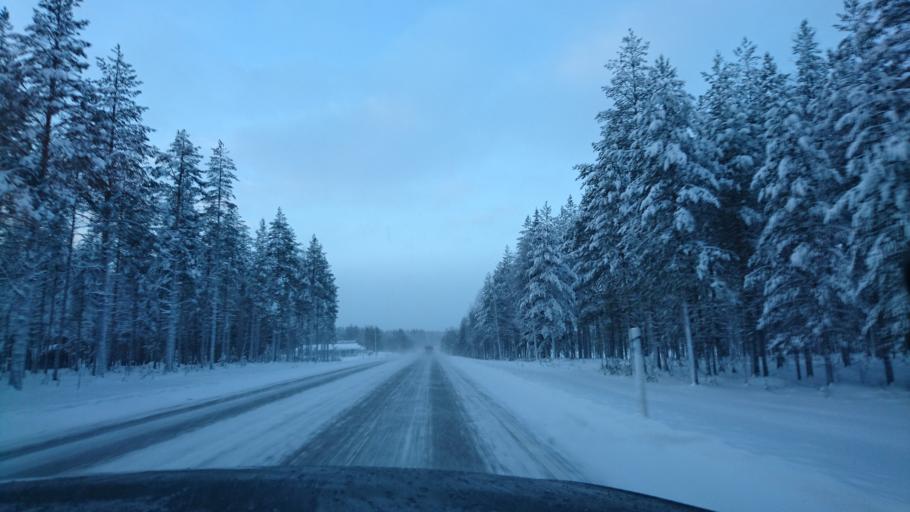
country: FI
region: Northern Ostrobothnia
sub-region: Koillismaa
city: Taivalkoski
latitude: 65.4869
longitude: 27.8547
